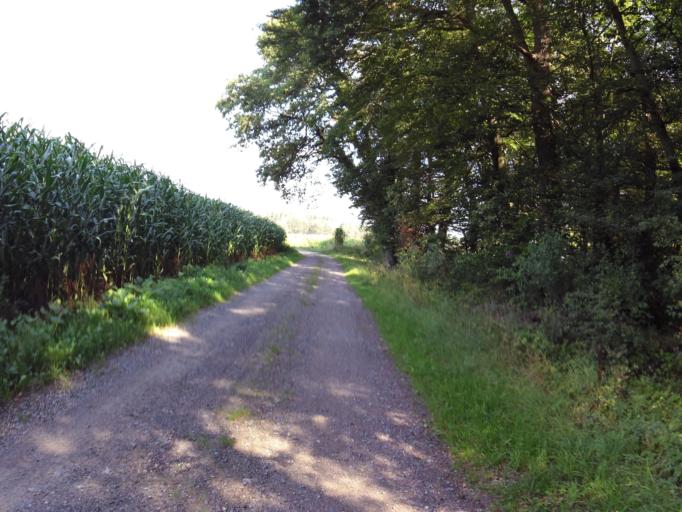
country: DE
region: North Rhine-Westphalia
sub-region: Regierungsbezirk Munster
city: Gescher
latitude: 52.0177
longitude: 6.9907
